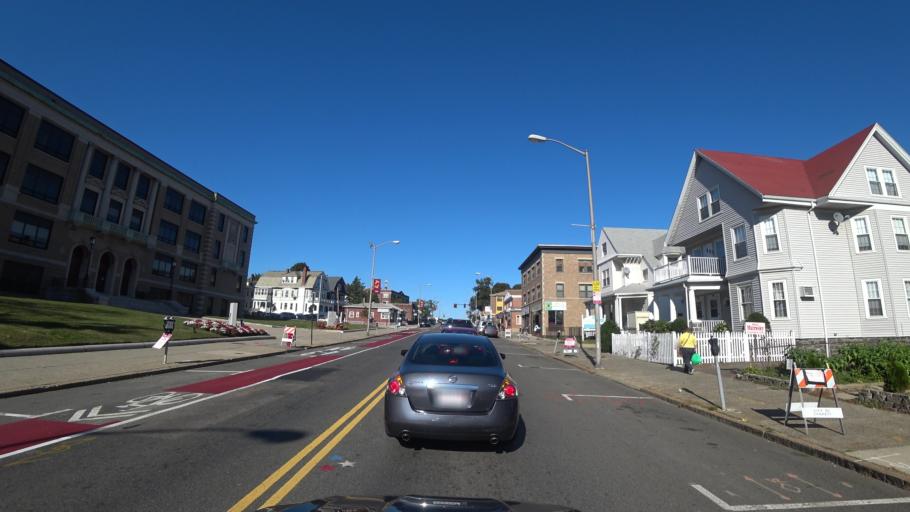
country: US
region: Massachusetts
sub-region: Middlesex County
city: Everett
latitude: 42.4098
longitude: -71.0529
